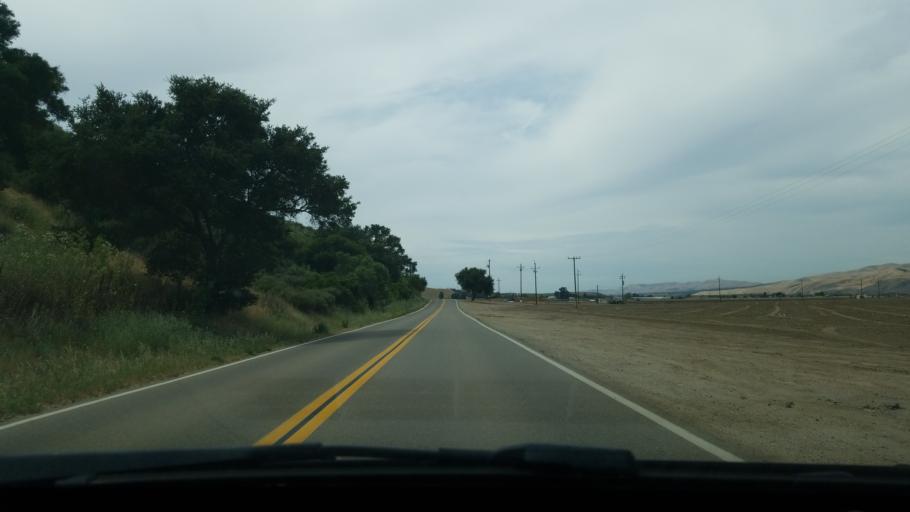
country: US
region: California
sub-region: Santa Barbara County
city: Los Alamos
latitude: 34.8709
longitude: -120.3021
